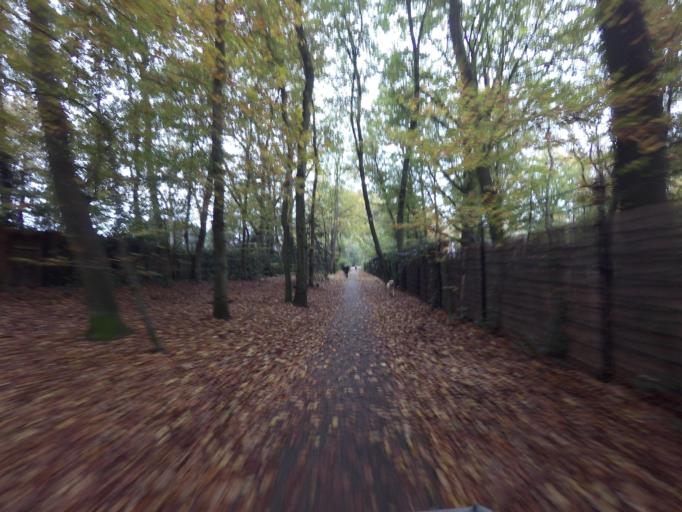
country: NL
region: North Holland
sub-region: Gemeente Hilversum
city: Hilversum
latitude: 52.2076
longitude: 5.1779
